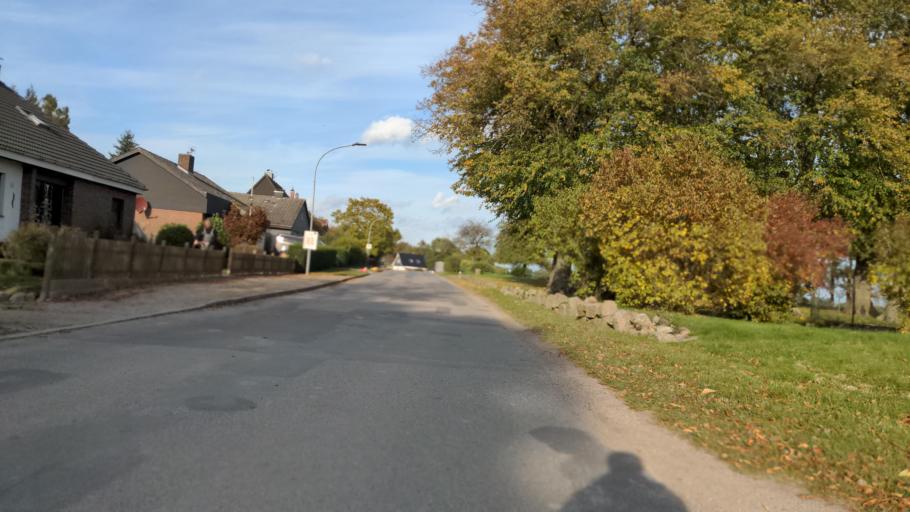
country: DE
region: Schleswig-Holstein
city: Ahrensbok
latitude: 53.9620
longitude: 10.5306
